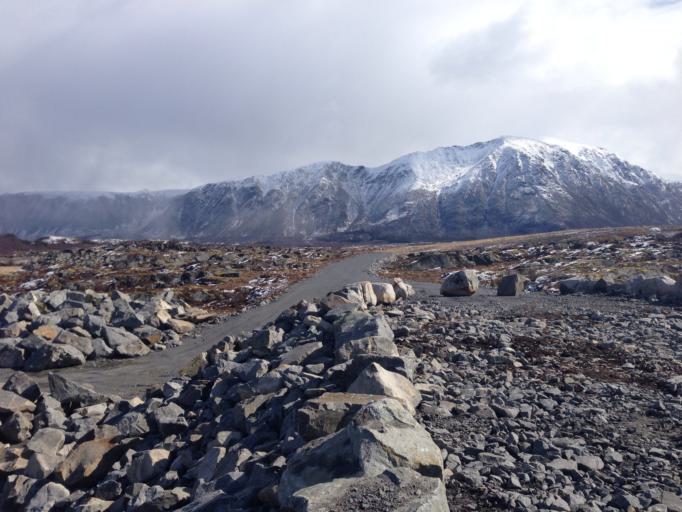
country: NO
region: Nordland
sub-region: Vagan
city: Kabelvag
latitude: 68.3838
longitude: 14.4106
